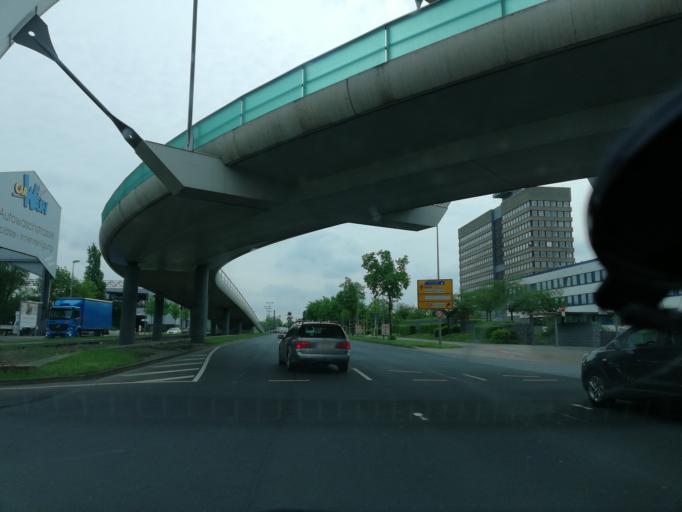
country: DE
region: North Rhine-Westphalia
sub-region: Regierungsbezirk Dusseldorf
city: Dusseldorf
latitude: 51.2096
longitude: 6.7581
